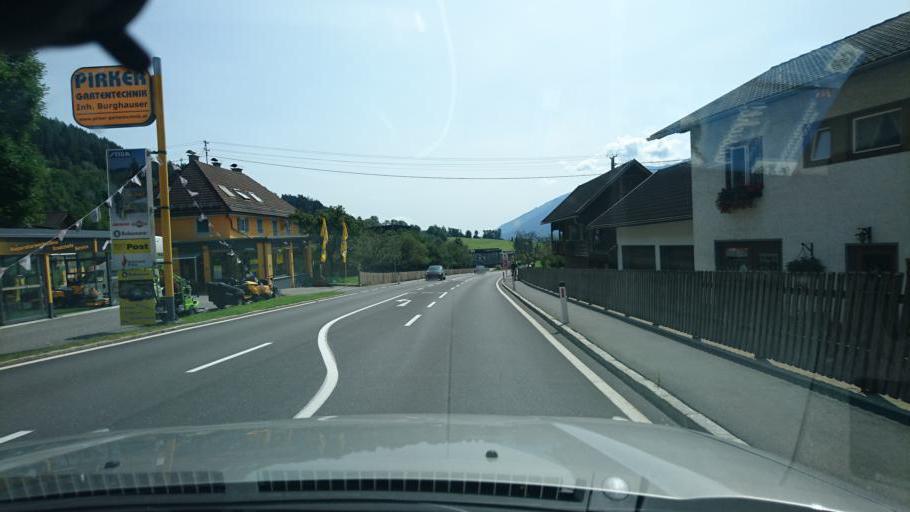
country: AT
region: Carinthia
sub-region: Politischer Bezirk Spittal an der Drau
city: Muhldorf
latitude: 46.8565
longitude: 13.3513
